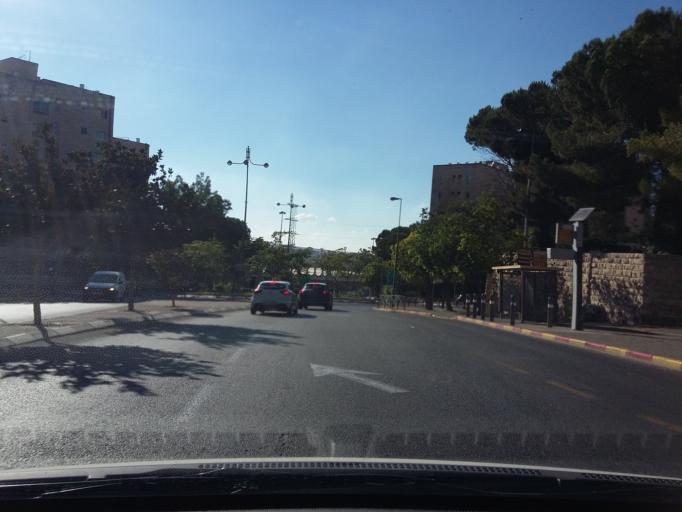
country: PS
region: West Bank
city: East Jerusalem
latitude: 31.8038
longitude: 35.2367
